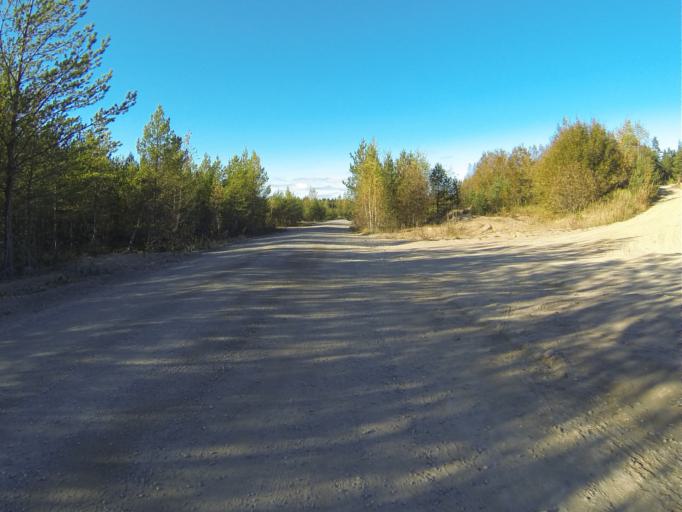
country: FI
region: Varsinais-Suomi
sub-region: Salo
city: Saerkisalo
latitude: 60.2221
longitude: 22.9879
